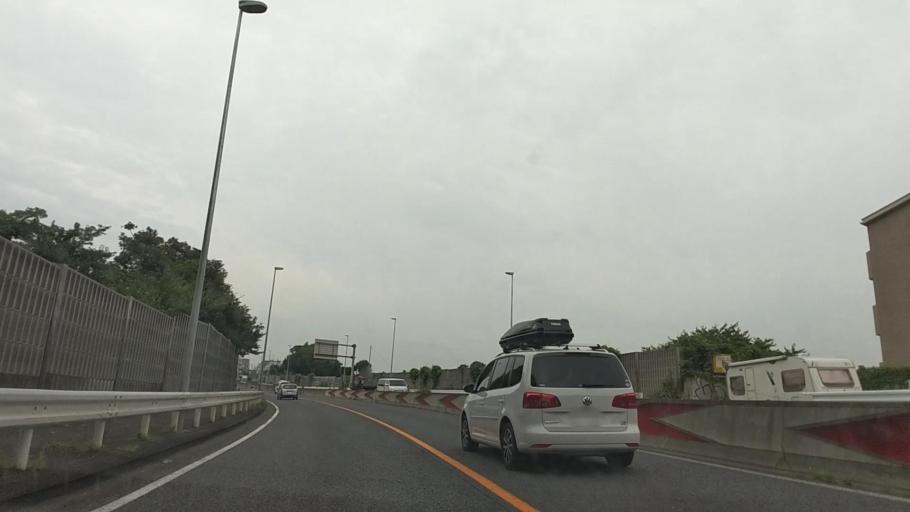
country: JP
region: Kanagawa
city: Fujisawa
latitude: 35.4116
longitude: 139.5317
